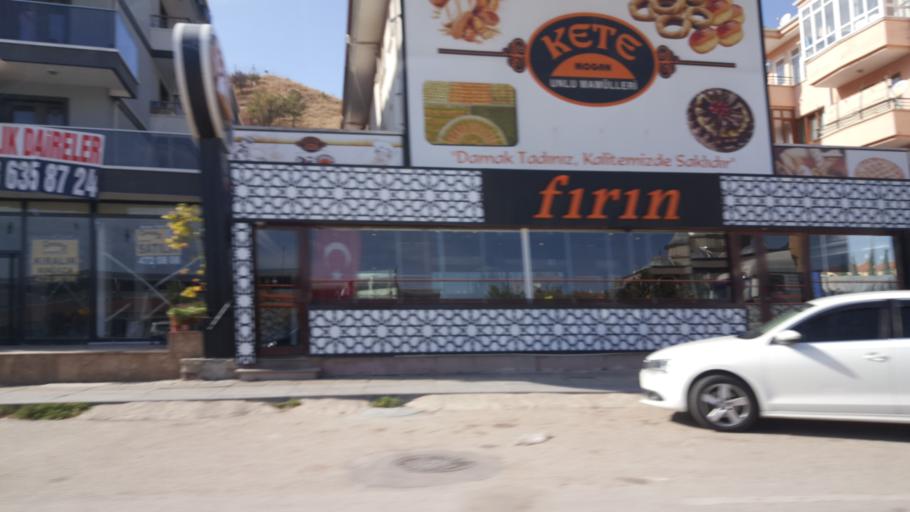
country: TR
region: Ankara
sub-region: Goelbasi
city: Golbasi
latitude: 39.8009
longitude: 32.7986
